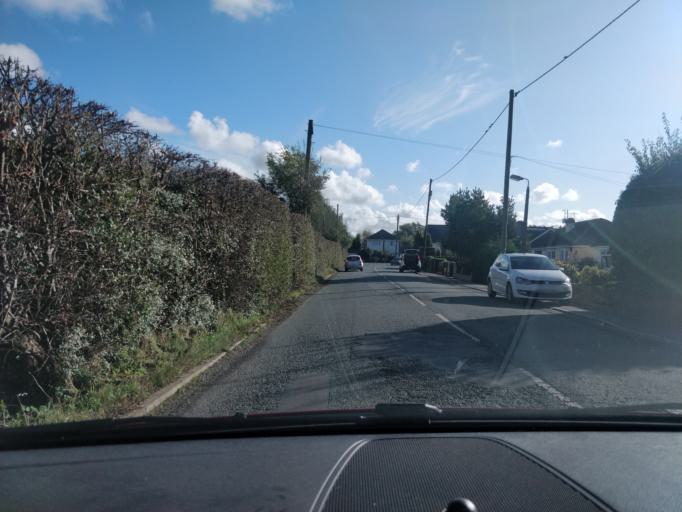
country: GB
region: England
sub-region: Lancashire
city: Banks
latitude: 53.6841
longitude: -2.9129
